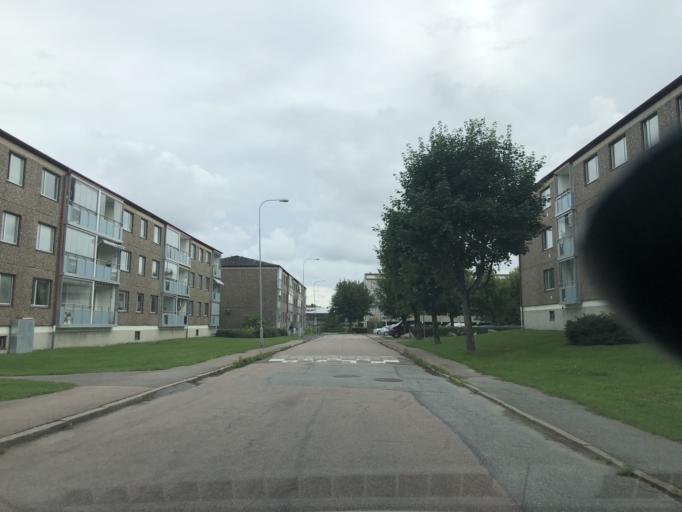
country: SE
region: Vaestra Goetaland
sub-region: Goteborg
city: Goeteborg
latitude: 57.7565
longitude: 11.9868
